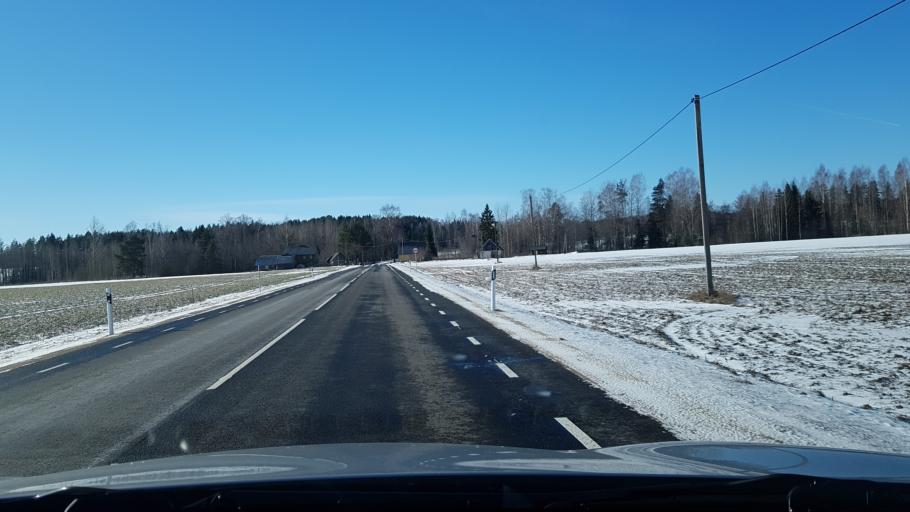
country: EE
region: Polvamaa
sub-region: Polva linn
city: Polva
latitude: 58.0934
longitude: 27.1460
